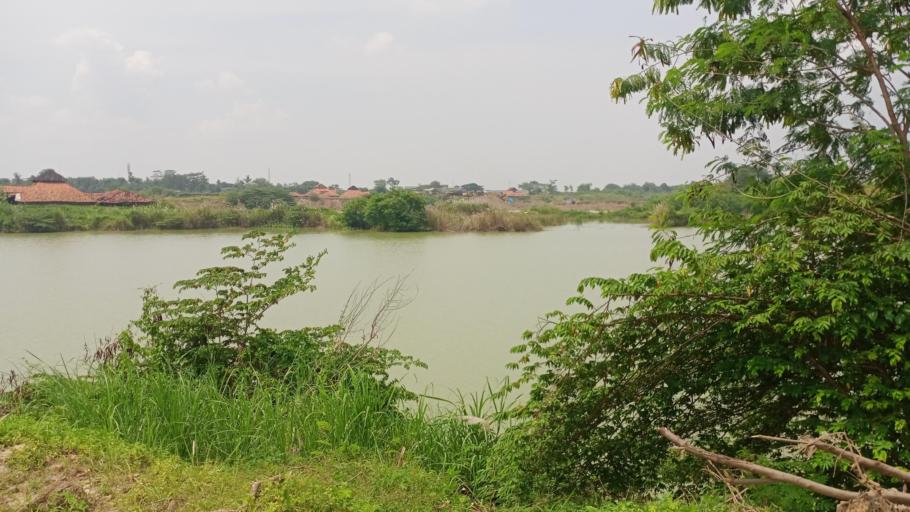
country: ID
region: West Java
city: Cileungsir
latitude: -6.4205
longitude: 107.1051
